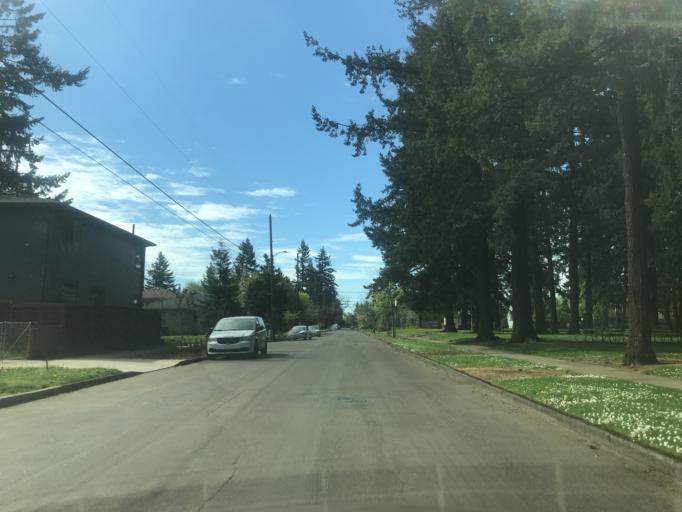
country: US
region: Oregon
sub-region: Multnomah County
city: Lents
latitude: 45.4814
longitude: -122.5867
